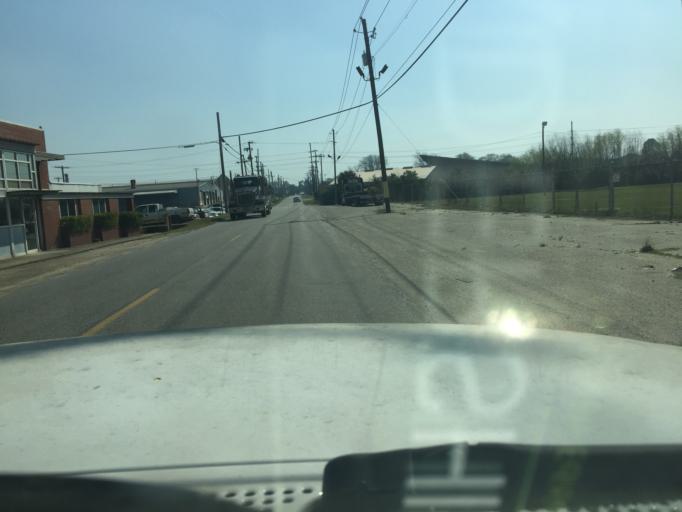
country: US
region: Georgia
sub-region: Chatham County
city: Savannah
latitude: 32.0918
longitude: -81.1111
